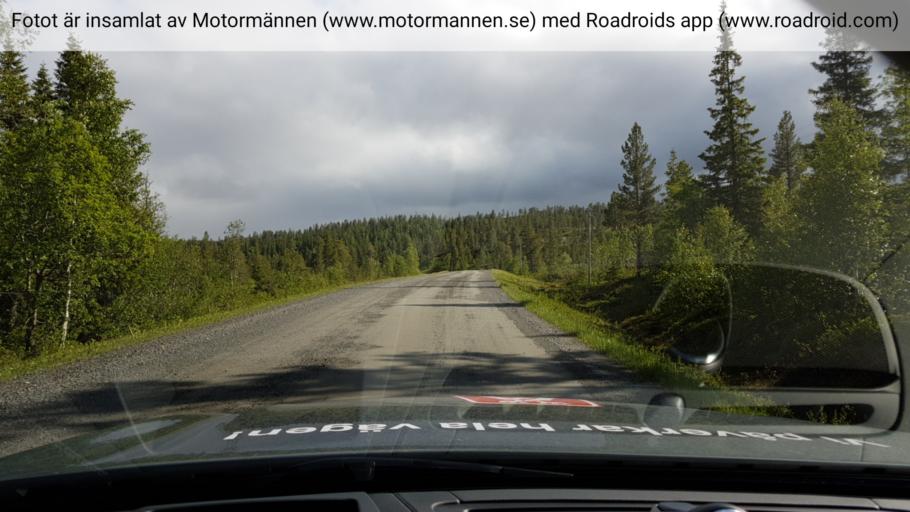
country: NO
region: Nord-Trondelag
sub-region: Snasa
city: Snaase
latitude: 63.7263
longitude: 12.4766
